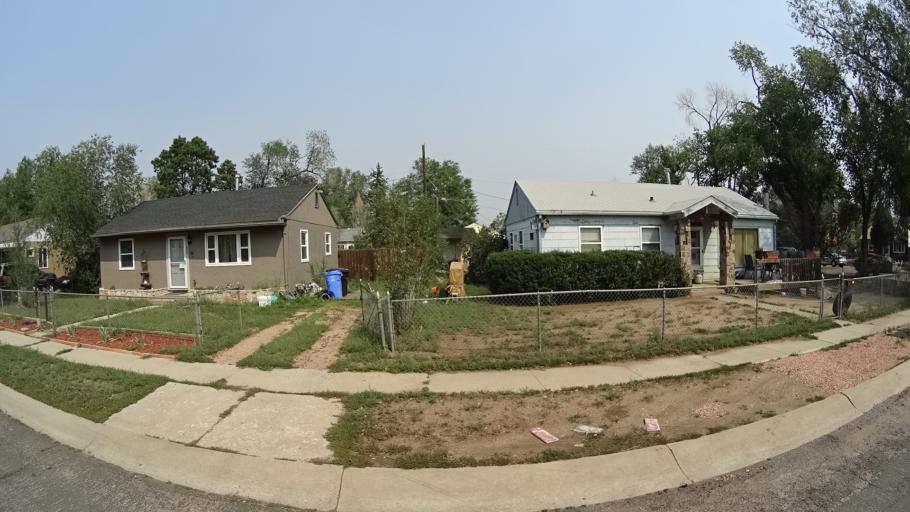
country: US
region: Colorado
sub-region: El Paso County
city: Colorado Springs
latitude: 38.8043
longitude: -104.8116
